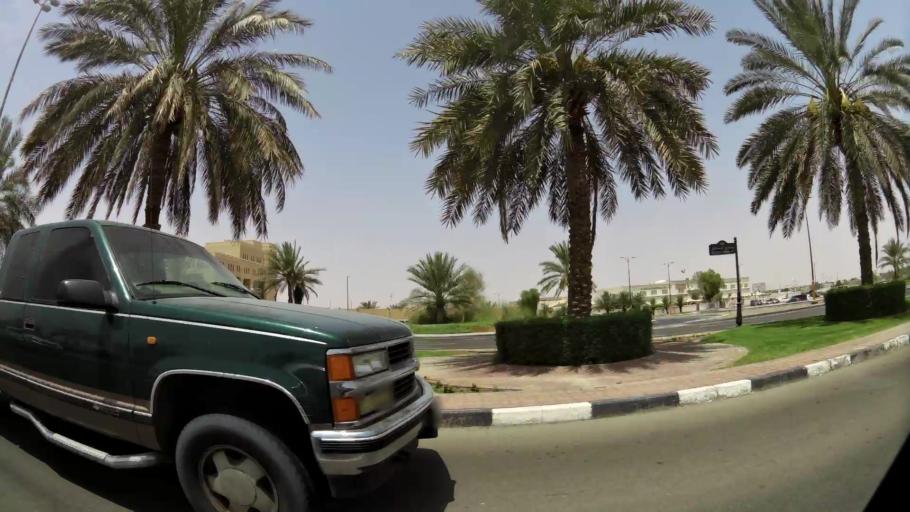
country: AE
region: Abu Dhabi
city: Al Ain
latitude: 24.2007
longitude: 55.7280
